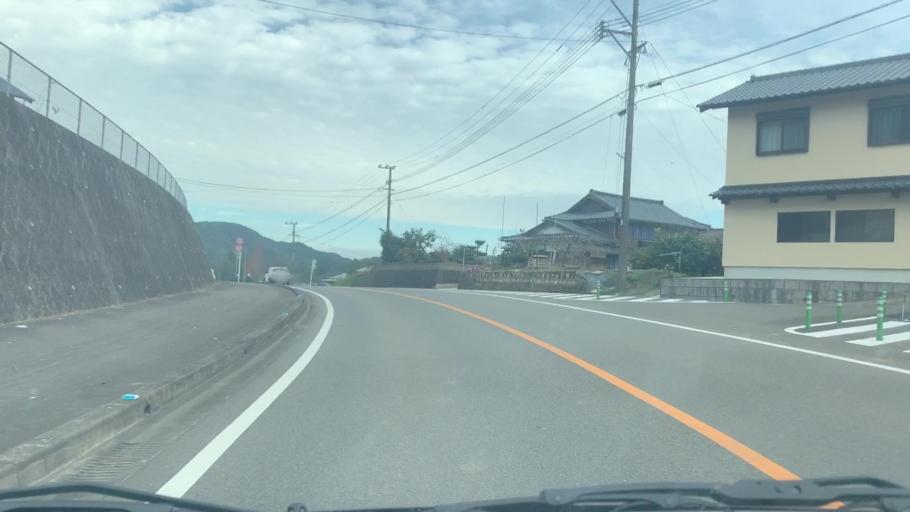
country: JP
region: Saga Prefecture
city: Takeocho-takeo
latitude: 33.2441
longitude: 129.9701
